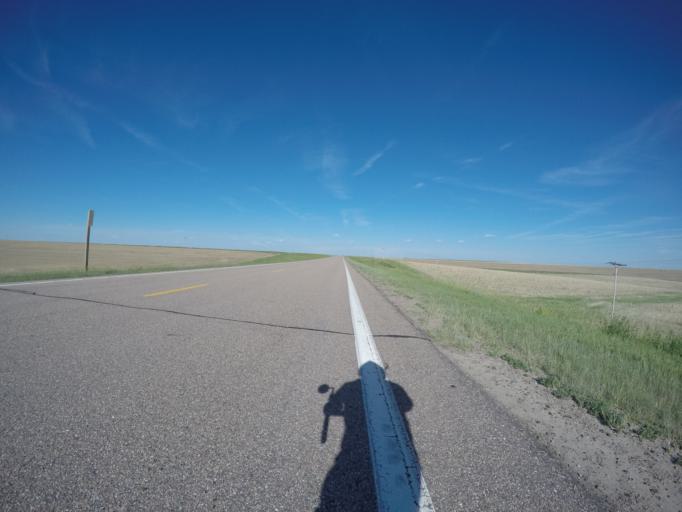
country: US
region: Kansas
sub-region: Cheyenne County
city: Saint Francis
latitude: 39.7566
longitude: -101.9777
